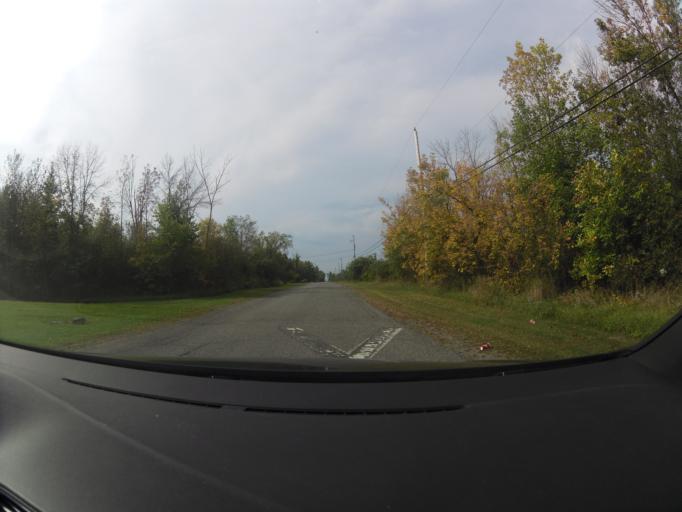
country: CA
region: Ontario
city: Bells Corners
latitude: 45.3981
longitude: -75.9820
